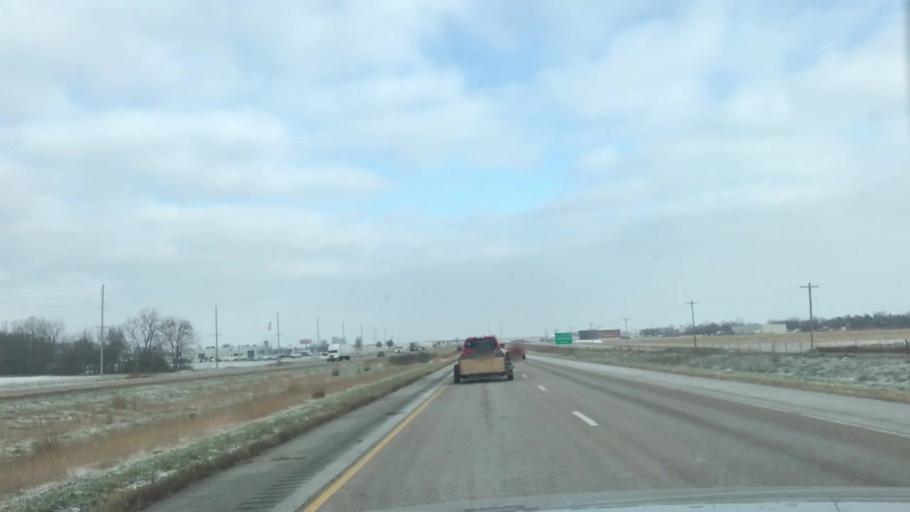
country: US
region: Illinois
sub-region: Macoupin County
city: Staunton
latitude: 39.0084
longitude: -89.7495
